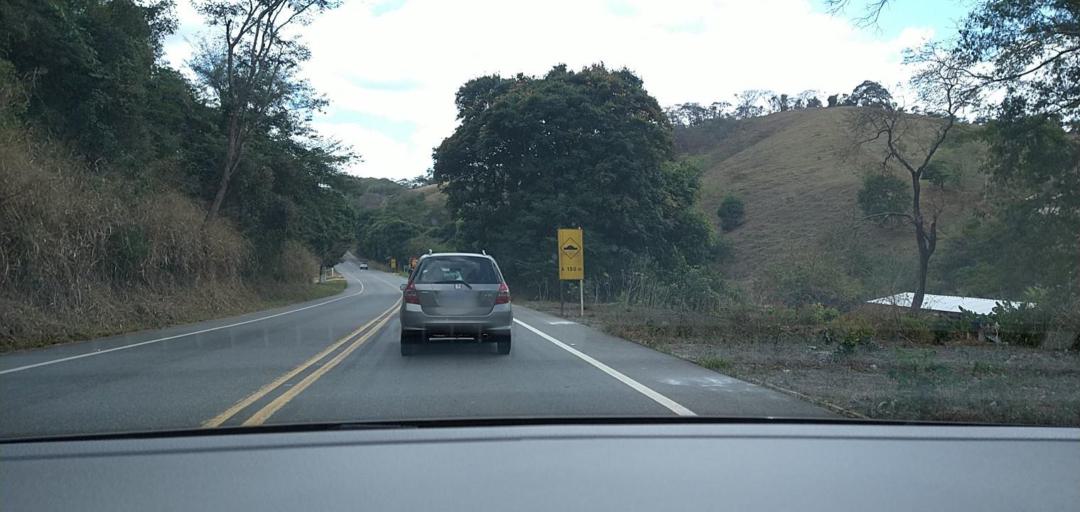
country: BR
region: Minas Gerais
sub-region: Ponte Nova
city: Ponte Nova
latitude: -20.5006
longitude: -42.8766
